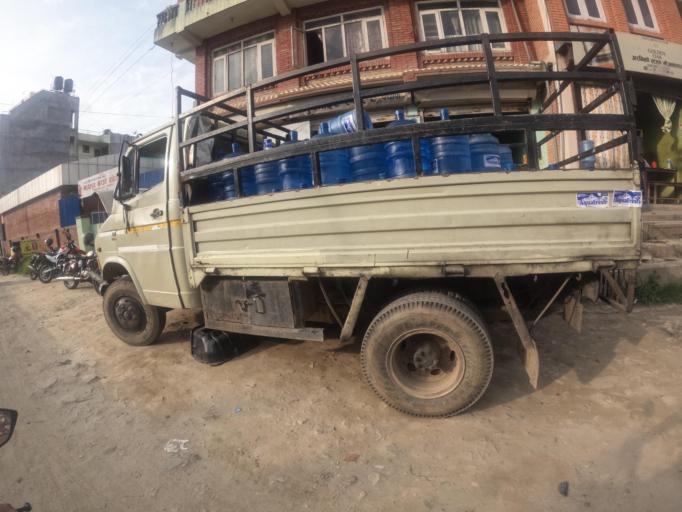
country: NP
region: Central Region
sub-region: Bagmati Zone
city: Bhaktapur
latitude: 27.6743
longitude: 85.3887
